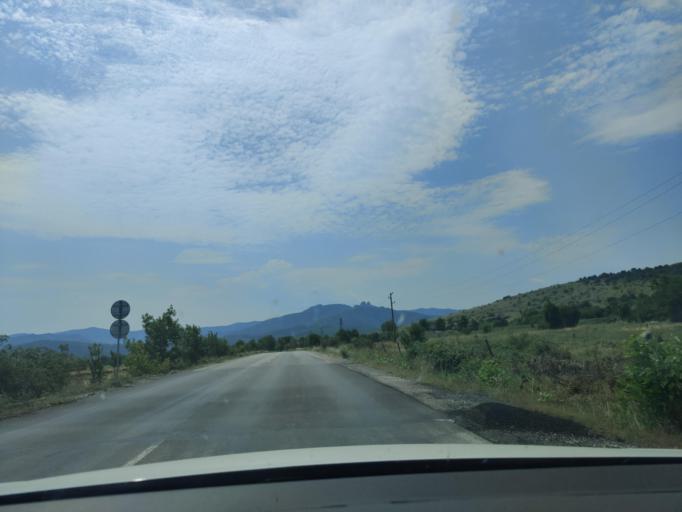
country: BG
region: Vidin
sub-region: Obshtina Ruzhintsi
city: Ruzhintsi
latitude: 43.5483
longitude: 22.9413
